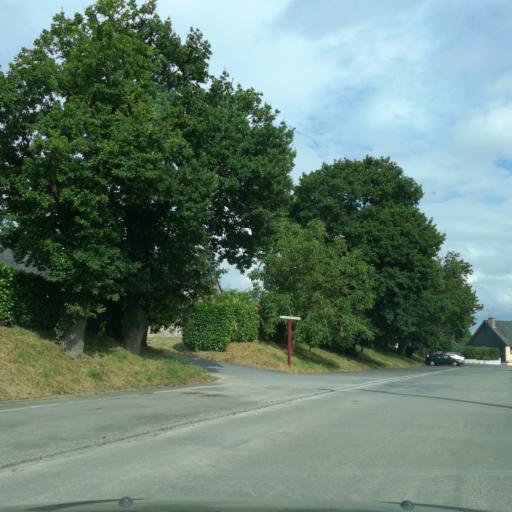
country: FR
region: Brittany
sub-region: Departement d'Ille-et-Vilaine
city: Montauban-de-Bretagne
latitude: 48.1963
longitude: -2.0472
